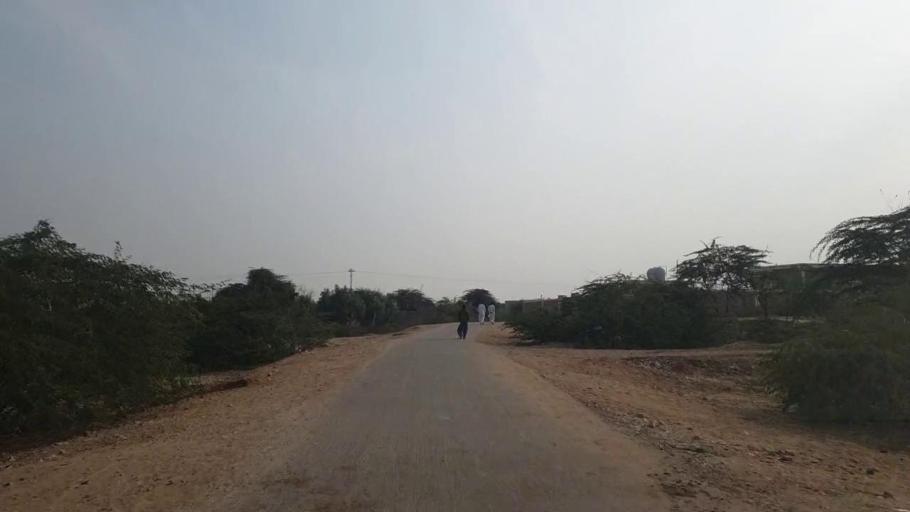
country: PK
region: Sindh
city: Sann
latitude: 26.0583
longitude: 68.1016
